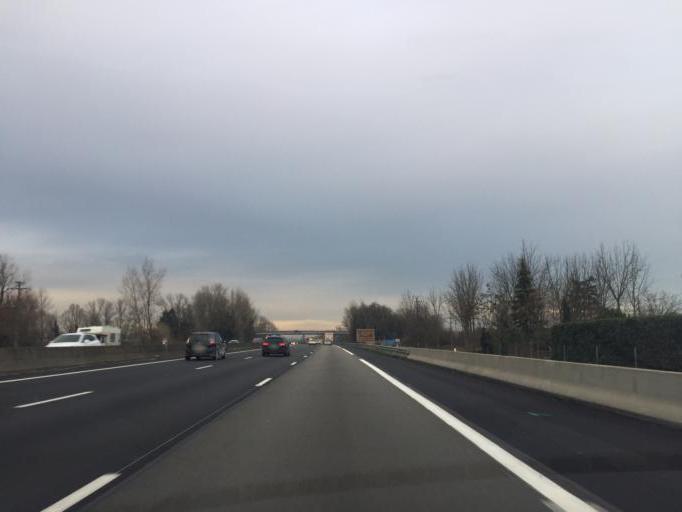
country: FR
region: Rhone-Alpes
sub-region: Departement du Rhone
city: Saint-Georges-de-Reneins
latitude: 46.0693
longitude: 4.7405
